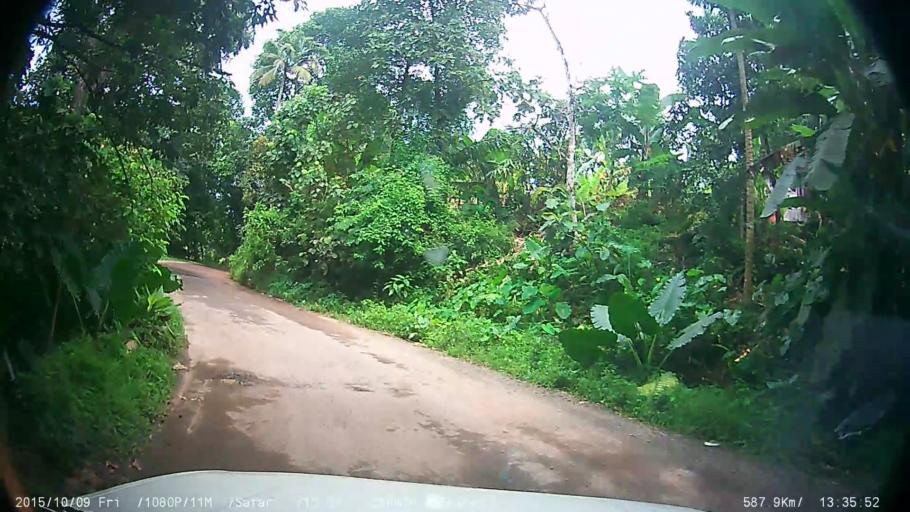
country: IN
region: Kerala
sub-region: Ernakulam
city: Piravam
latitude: 9.8994
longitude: 76.5601
